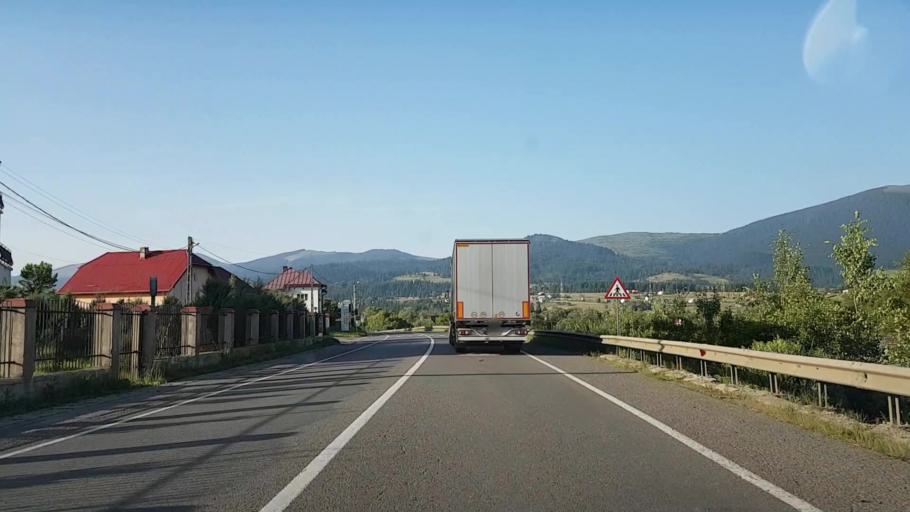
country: RO
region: Suceava
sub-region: Comuna Cosna
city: Cosna
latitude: 47.3560
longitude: 25.1878
